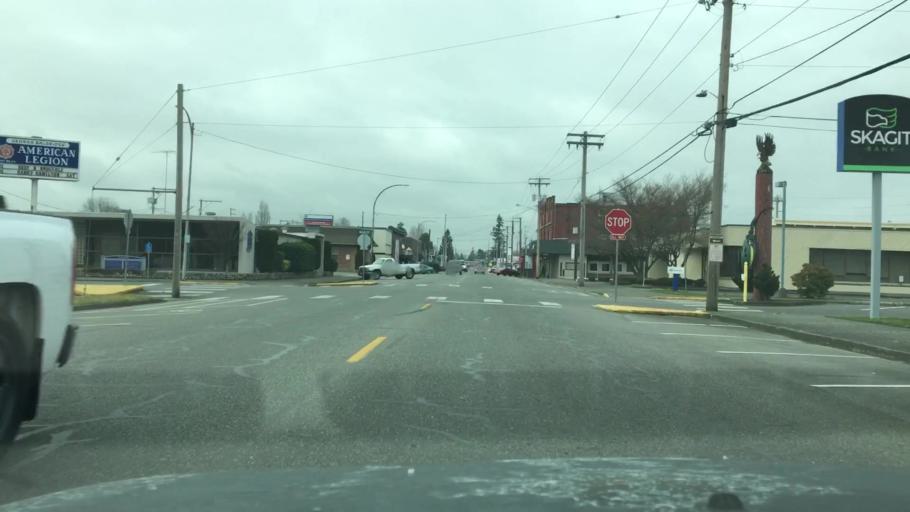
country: US
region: Washington
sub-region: Skagit County
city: Sedro-Woolley
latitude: 48.5054
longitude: -122.2362
